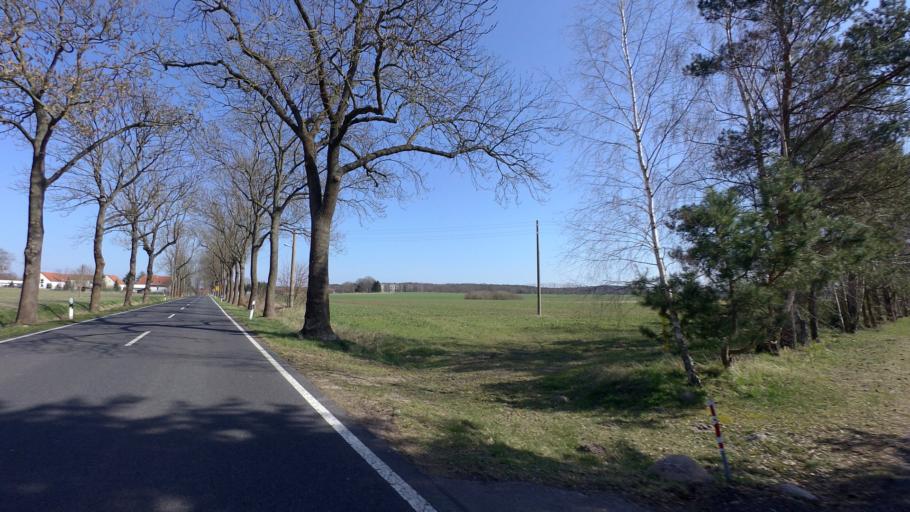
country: DE
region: Brandenburg
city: Schonermark
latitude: 53.0061
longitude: 13.1099
